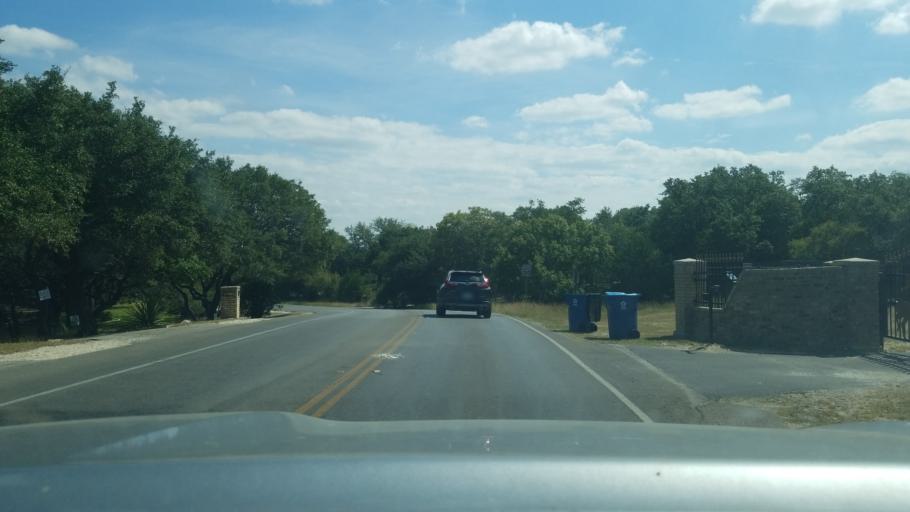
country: US
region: Texas
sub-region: Bexar County
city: Fair Oaks Ranch
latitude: 29.7313
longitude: -98.6335
